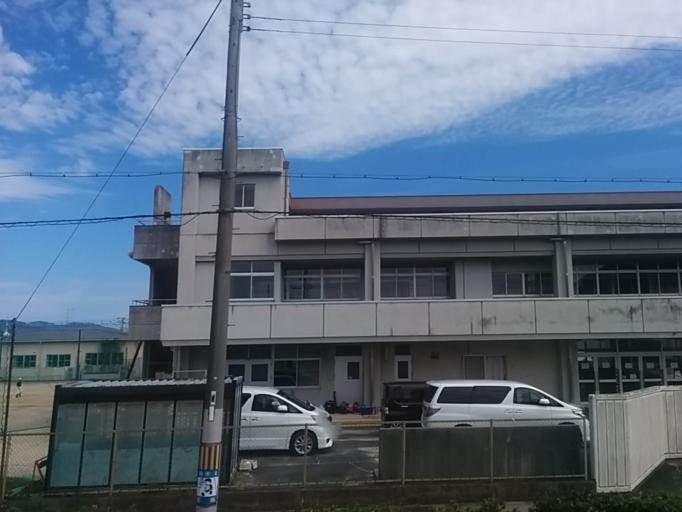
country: JP
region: Nara
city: Kashihara-shi
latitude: 34.4969
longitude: 135.7943
